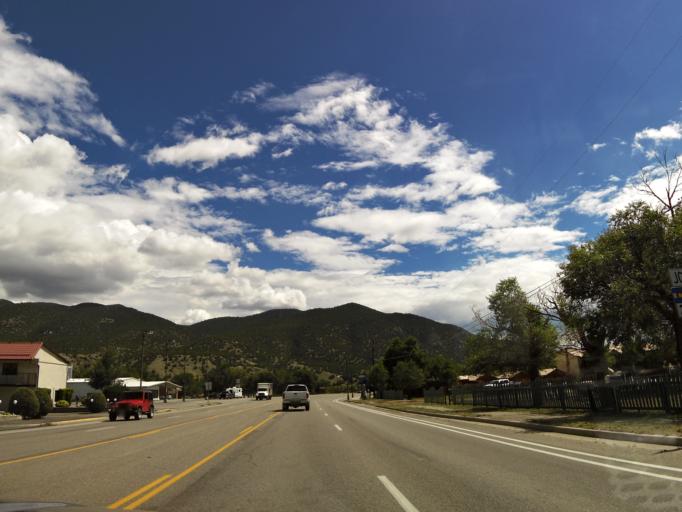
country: US
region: Colorado
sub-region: Chaffee County
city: Salida
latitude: 38.5240
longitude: -105.9878
